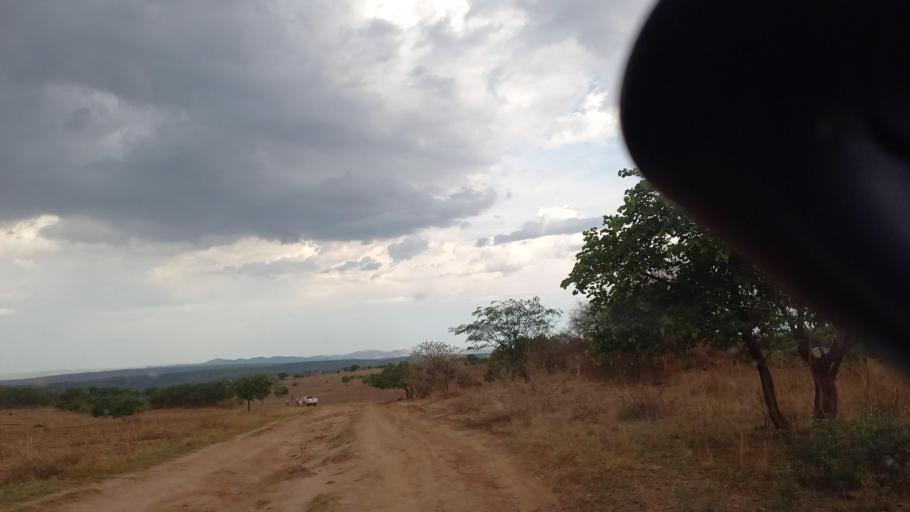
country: ZM
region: Lusaka
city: Kafue
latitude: -16.1353
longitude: 28.0549
